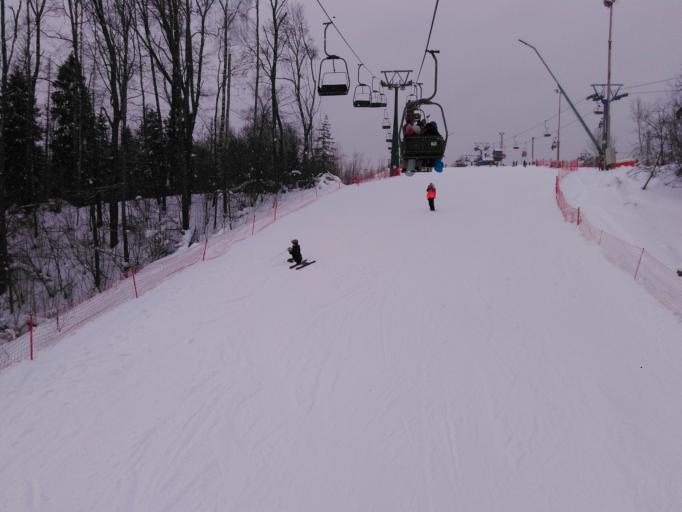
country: RU
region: Moskovskaya
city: Yakhroma
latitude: 56.2585
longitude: 37.4328
